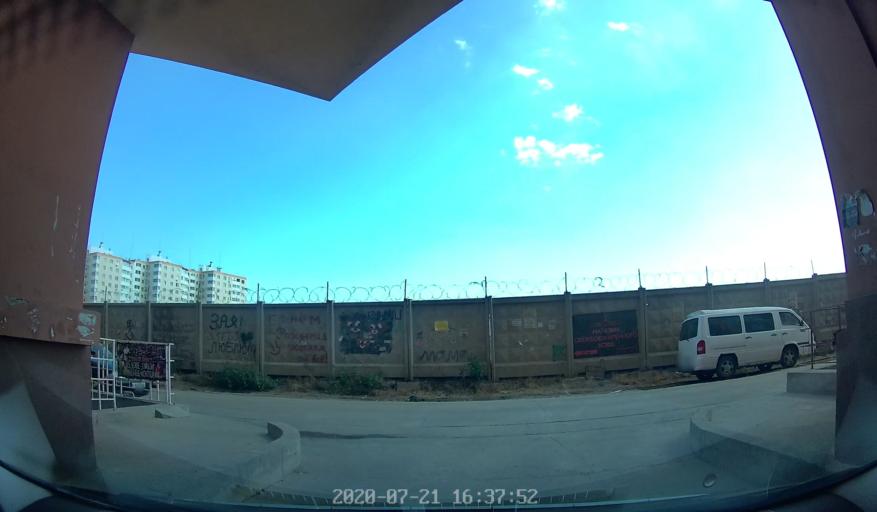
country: TR
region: Kirklareli
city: Sergen
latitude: 41.7605
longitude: 27.6347
